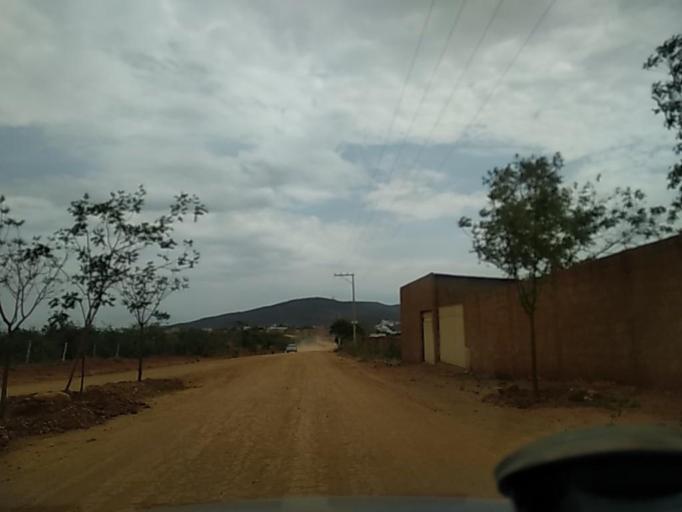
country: BR
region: Bahia
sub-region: Caetite
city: Caetite
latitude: -14.0473
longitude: -42.4733
